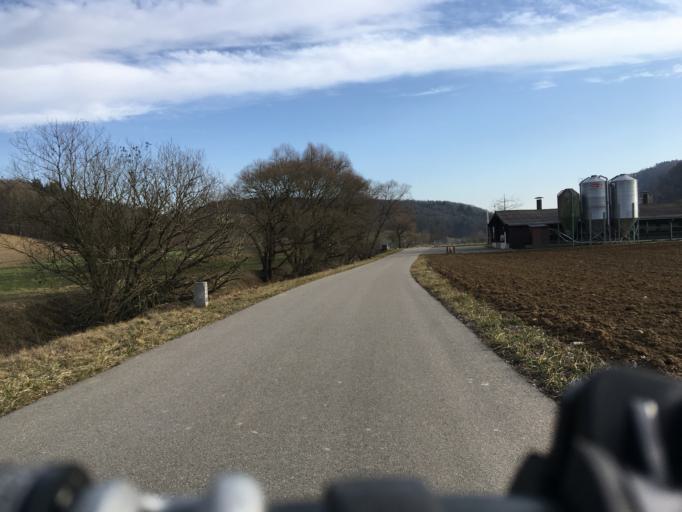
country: CH
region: Schaffhausen
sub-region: Bezirk Reiat
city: Thayngen
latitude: 47.7707
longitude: 8.6833
